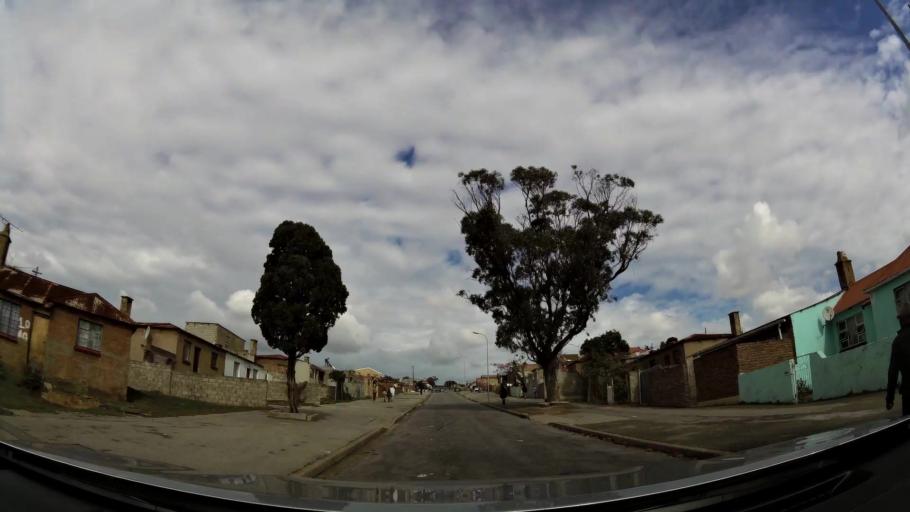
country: ZA
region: Eastern Cape
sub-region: Nelson Mandela Bay Metropolitan Municipality
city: Port Elizabeth
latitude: -33.9319
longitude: 25.5732
